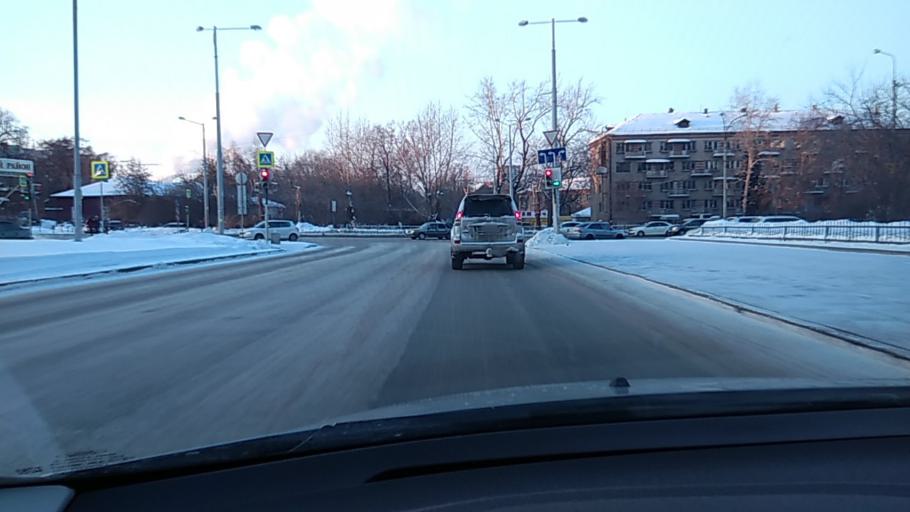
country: RU
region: Sverdlovsk
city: Yekaterinburg
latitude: 56.8455
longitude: 60.5876
